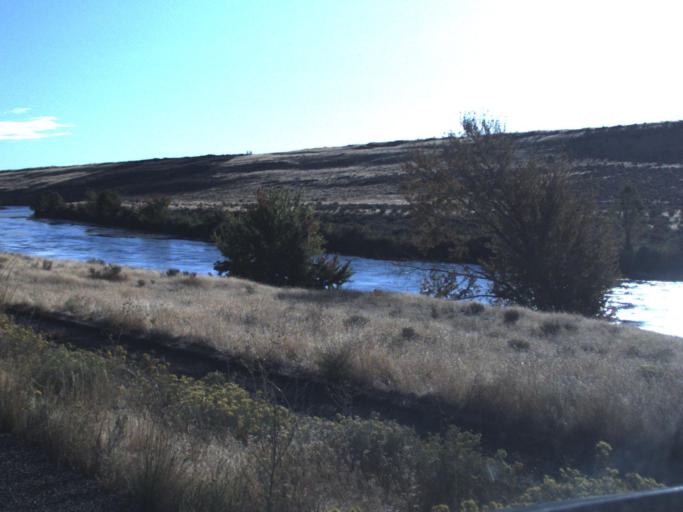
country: US
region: Washington
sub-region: Benton County
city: Benton City
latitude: 46.3508
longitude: -119.4641
